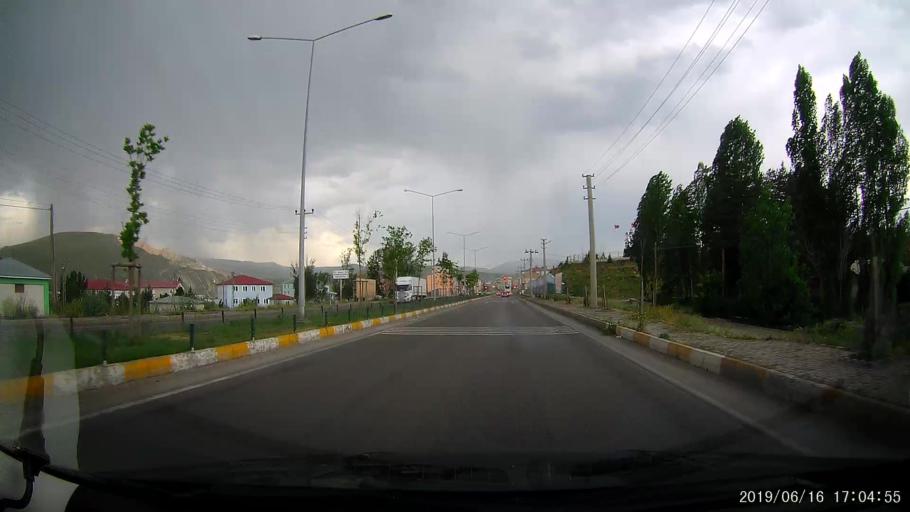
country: TR
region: Erzurum
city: Askale
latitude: 39.9231
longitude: 40.7033
